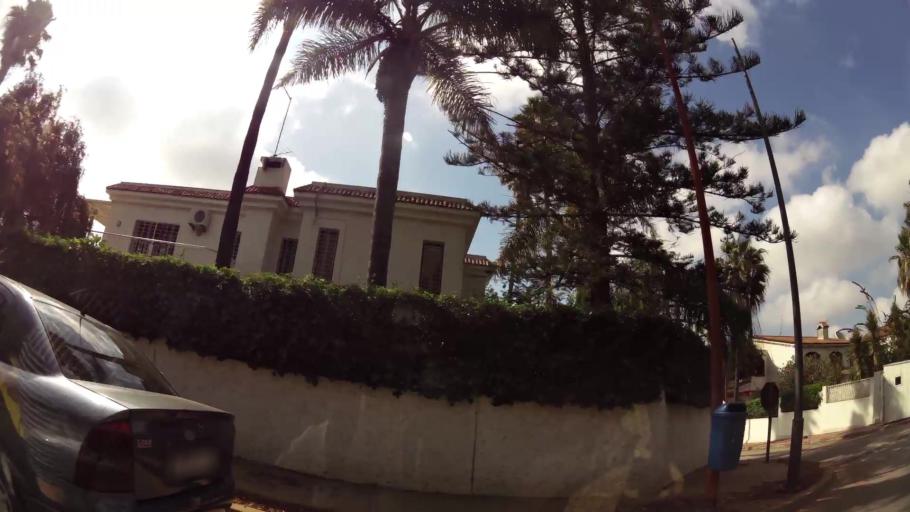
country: MA
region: Rabat-Sale-Zemmour-Zaer
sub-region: Skhirate-Temara
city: Temara
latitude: 33.9590
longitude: -6.8593
